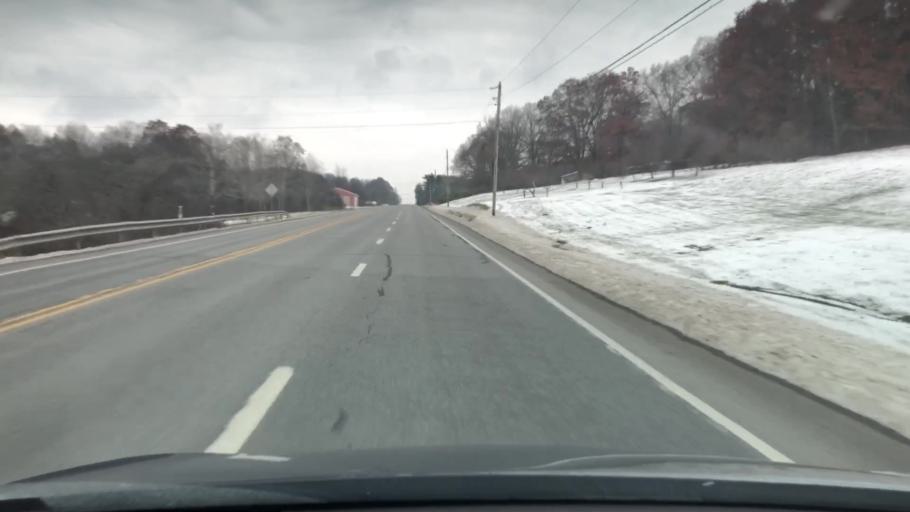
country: US
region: Pennsylvania
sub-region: Jefferson County
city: Brookville
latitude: 41.1492
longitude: -79.1266
